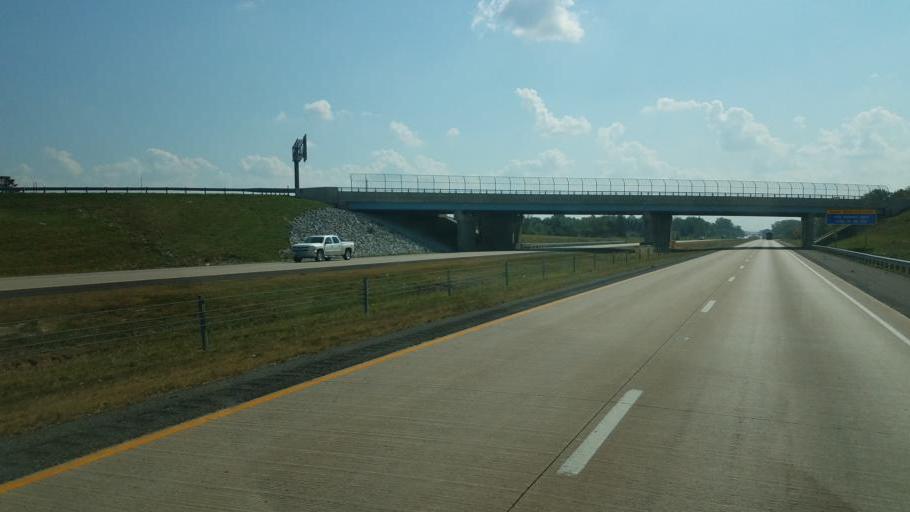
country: US
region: Indiana
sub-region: DeKalb County
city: Auburn
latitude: 41.3285
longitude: -85.0880
